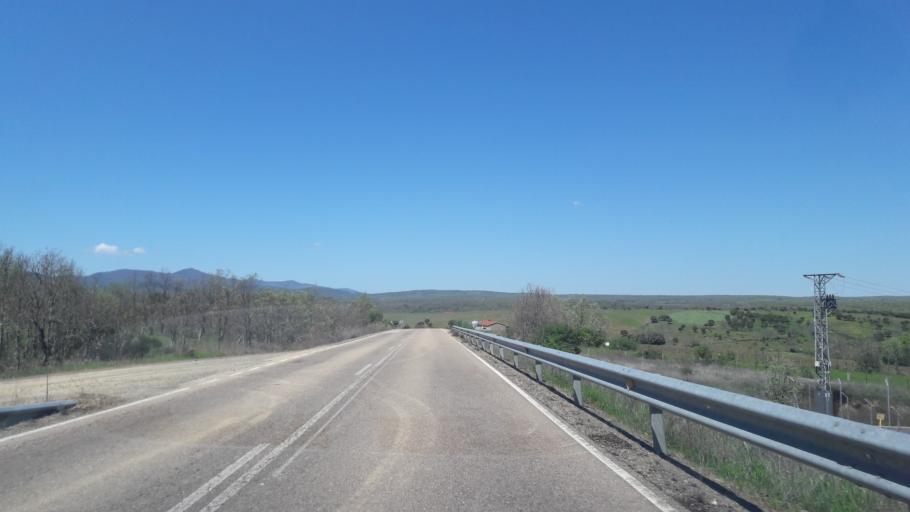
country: ES
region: Castille and Leon
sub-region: Provincia de Salamanca
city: Monleon
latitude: 40.5905
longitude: -5.8261
